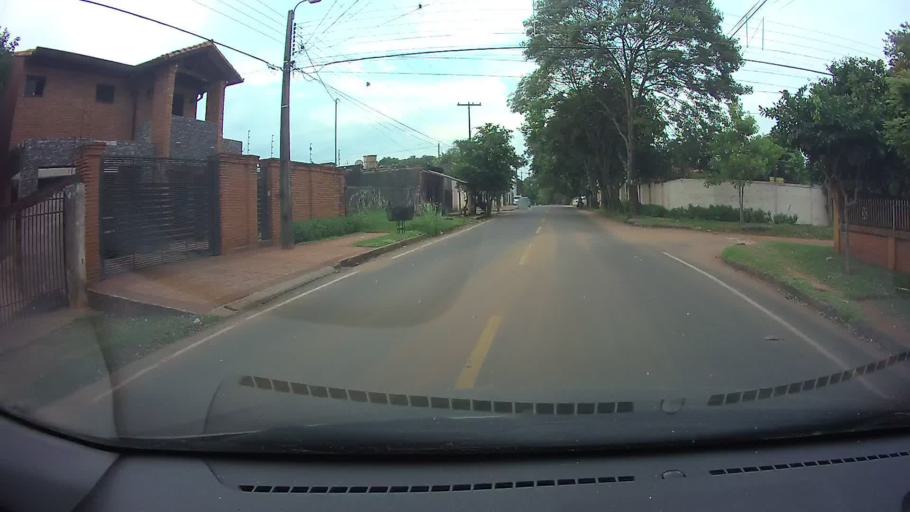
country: PY
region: Central
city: San Lorenzo
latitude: -25.2786
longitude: -57.4789
